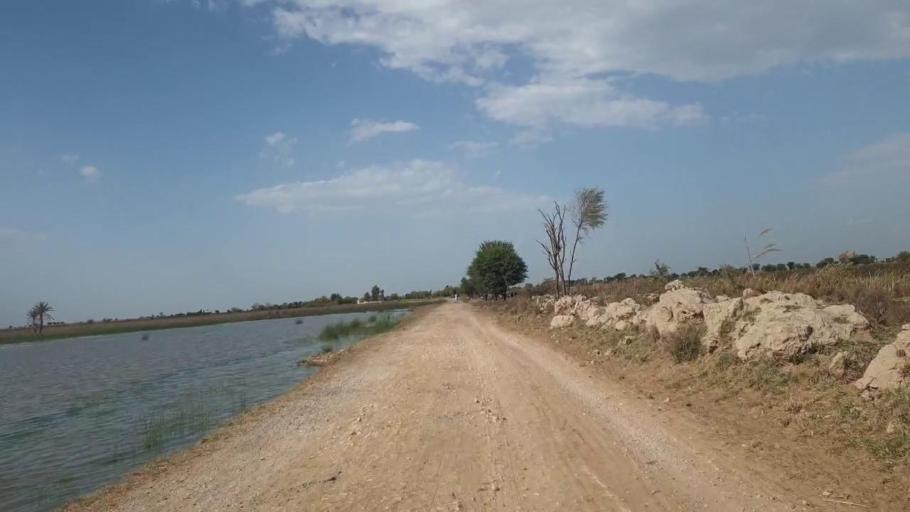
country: PK
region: Sindh
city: Shahdadpur
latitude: 25.9992
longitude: 68.4615
